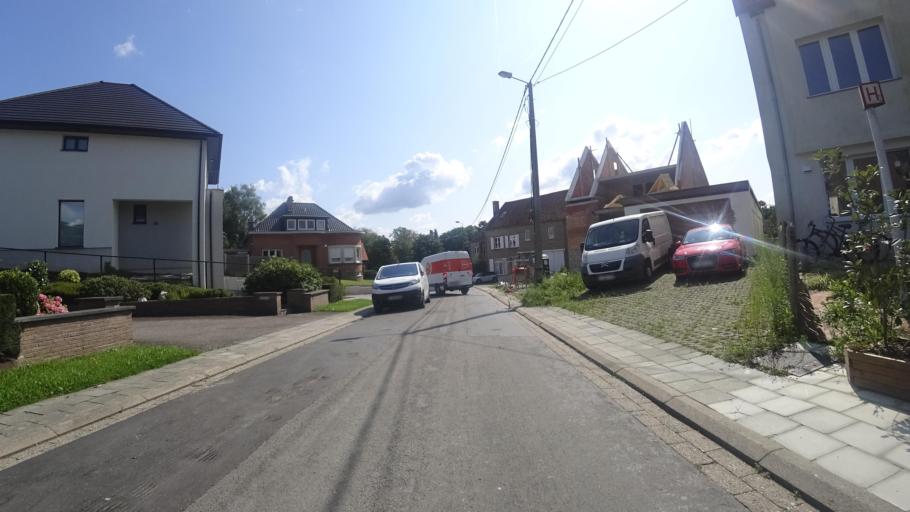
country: BE
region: Flanders
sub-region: Provincie Vlaams-Brabant
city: Tervuren
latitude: 50.8344
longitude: 4.5229
